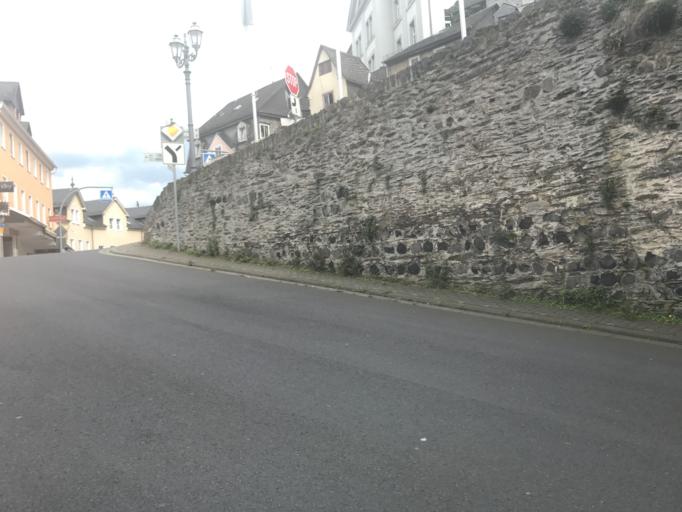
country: DE
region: Hesse
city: Weilburg
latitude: 50.4873
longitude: 8.2598
